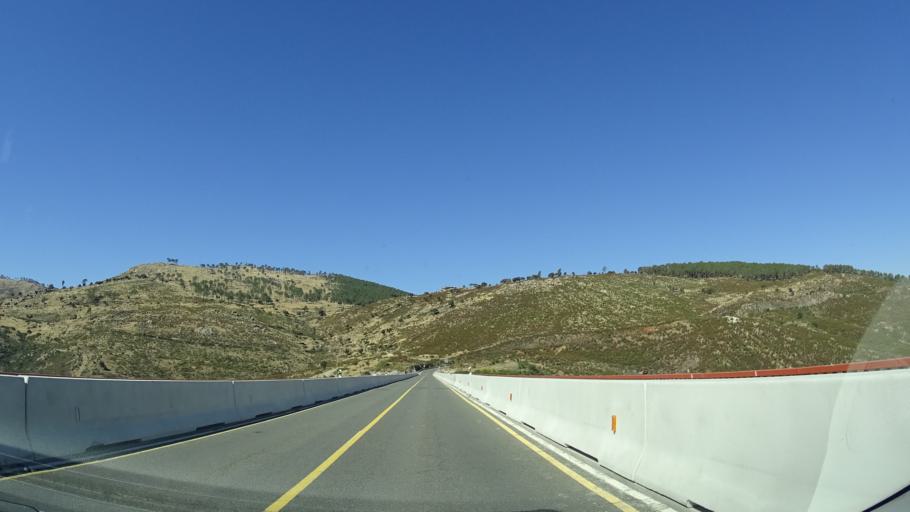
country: ES
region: Madrid
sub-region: Provincia de Madrid
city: Santa Maria de la Alameda
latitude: 40.5546
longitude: -4.2672
